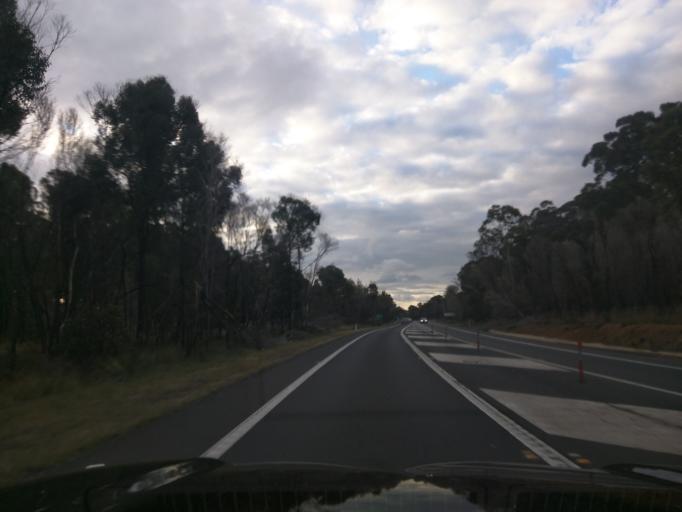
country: AU
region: New South Wales
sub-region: Wollondilly
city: Douglas Park
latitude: -34.3072
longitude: 150.7384
